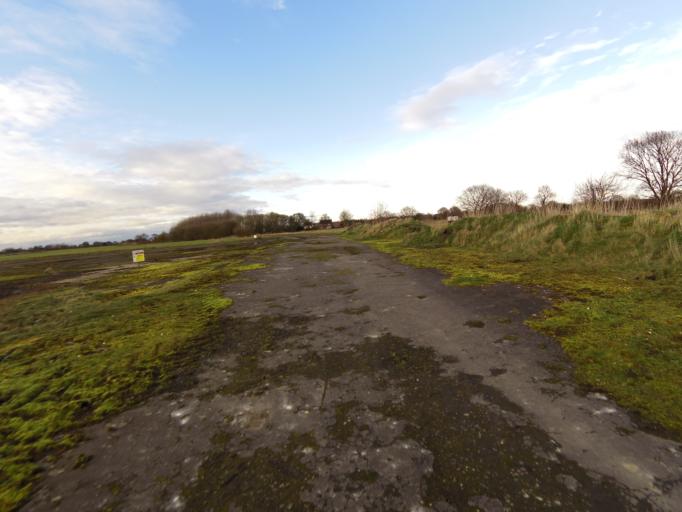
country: GB
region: England
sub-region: North Yorkshire
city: Brayton
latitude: 53.7513
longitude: -1.0785
